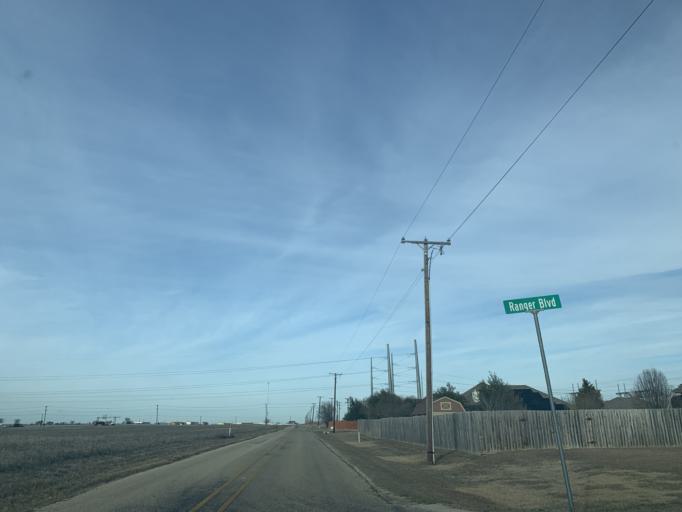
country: US
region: Texas
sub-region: Bell County
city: Salado
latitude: 30.9694
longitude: -97.5144
